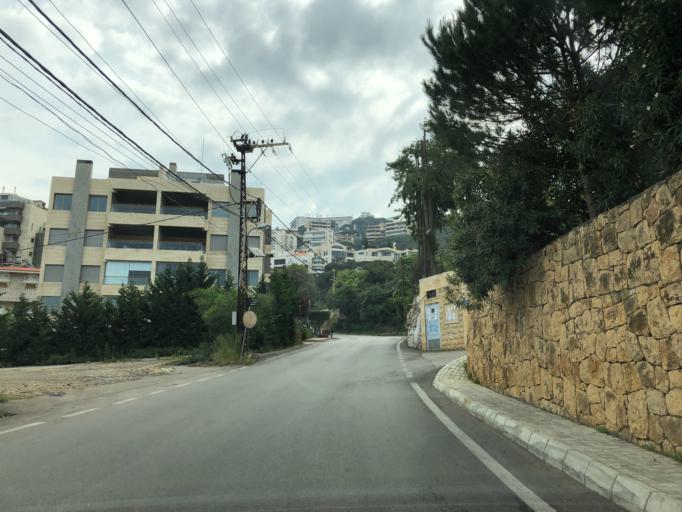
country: LB
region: Mont-Liban
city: Jdaidet el Matn
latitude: 33.8600
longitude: 35.5953
